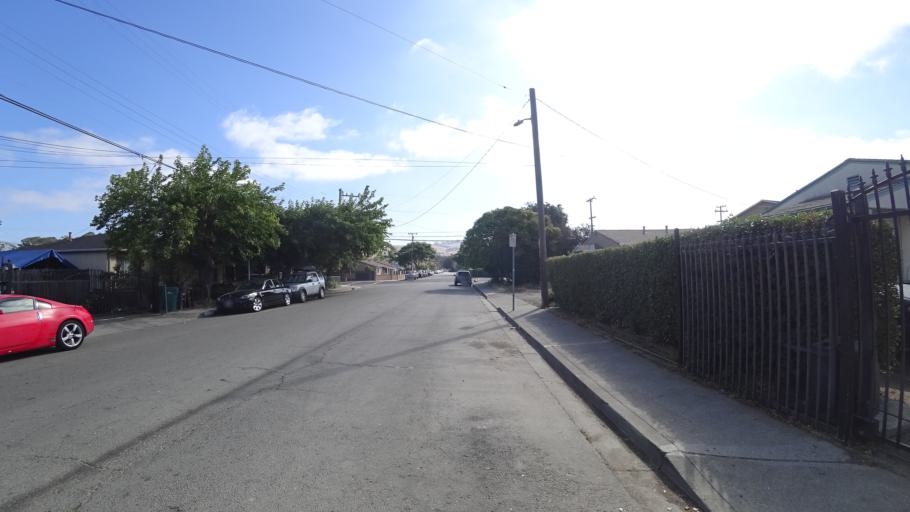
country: US
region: California
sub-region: Alameda County
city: Hayward
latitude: 37.6380
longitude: -122.0722
